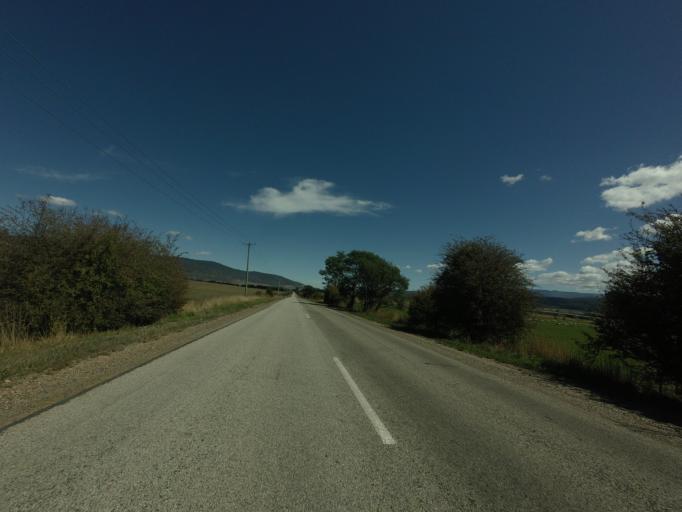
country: AU
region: Tasmania
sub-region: Break O'Day
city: St Helens
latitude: -41.6199
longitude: 148.0033
